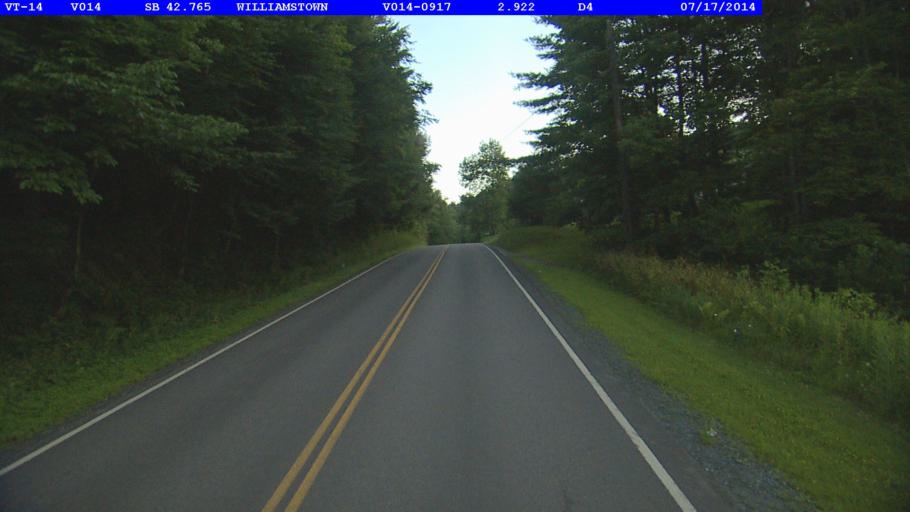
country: US
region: Vermont
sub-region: Orange County
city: Williamstown
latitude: 44.1006
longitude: -72.5452
